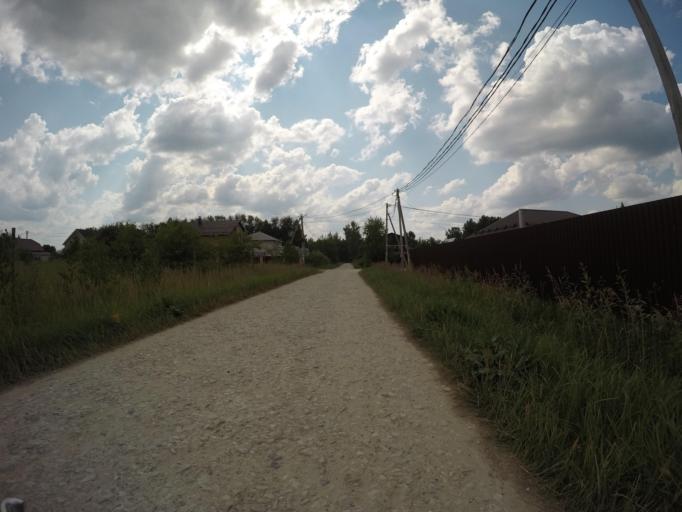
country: RU
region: Moskovskaya
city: Rechitsy
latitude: 55.6056
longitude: 38.5069
